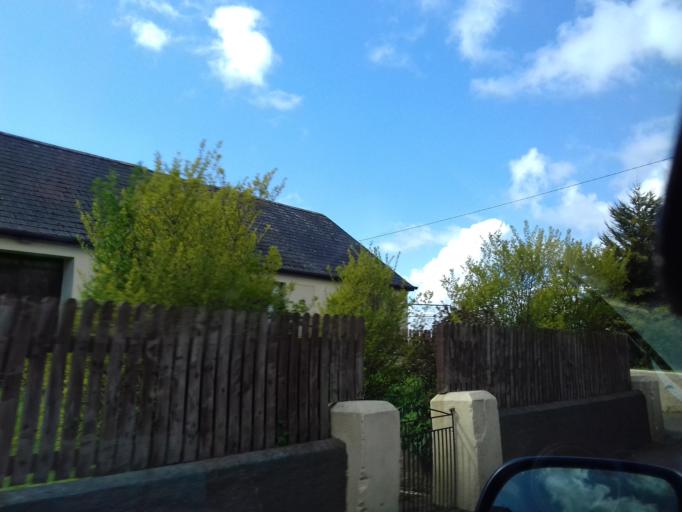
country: IE
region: Leinster
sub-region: Loch Garman
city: Castlebridge
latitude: 52.3930
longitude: -6.3889
